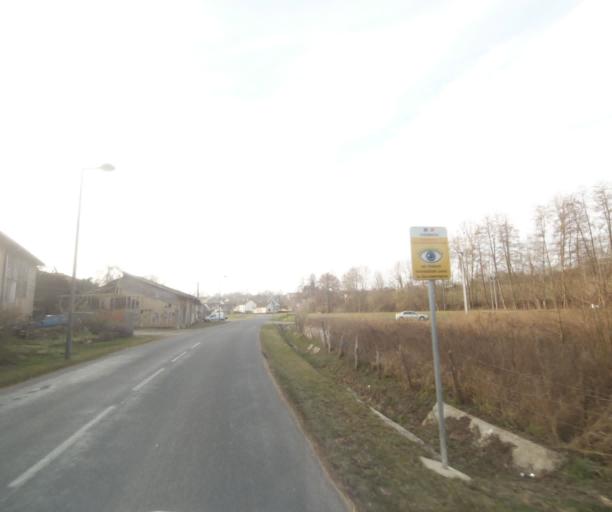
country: FR
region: Champagne-Ardenne
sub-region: Departement de la Marne
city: Sermaize-les-Bains
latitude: 48.7404
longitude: 4.9072
